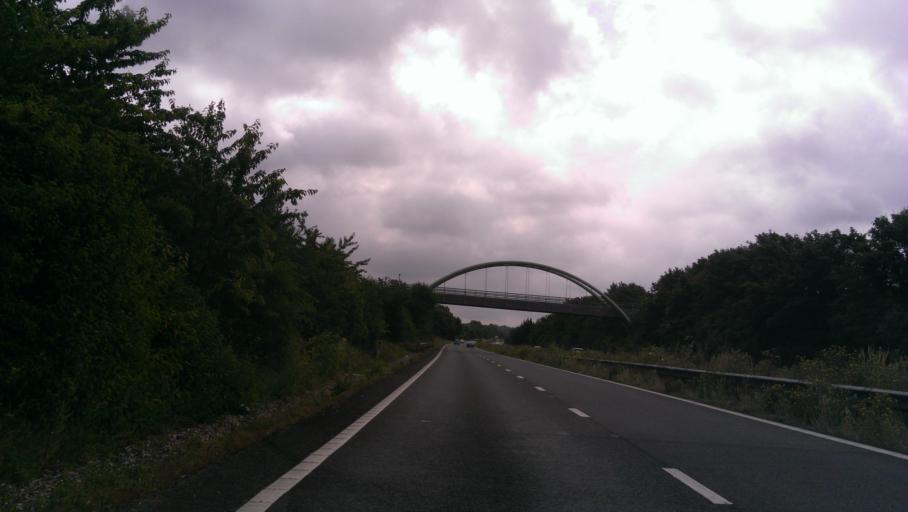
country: GB
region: England
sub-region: Kent
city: Barham
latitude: 51.2201
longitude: 1.1574
